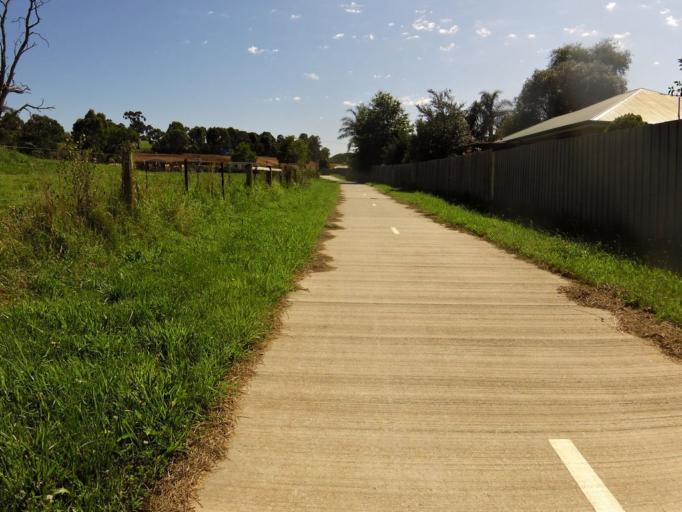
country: AU
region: Victoria
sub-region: Yarra Ranges
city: Kilsyth
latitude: -37.7767
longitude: 145.3324
